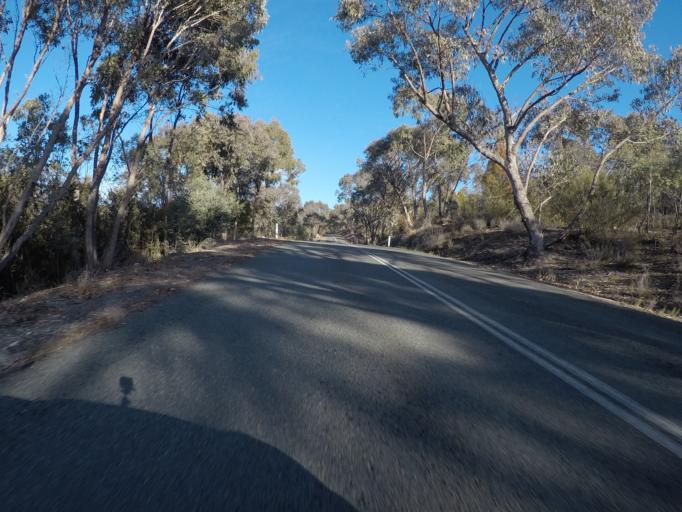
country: AU
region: Australian Capital Territory
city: Macarthur
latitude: -35.4647
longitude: 148.9662
